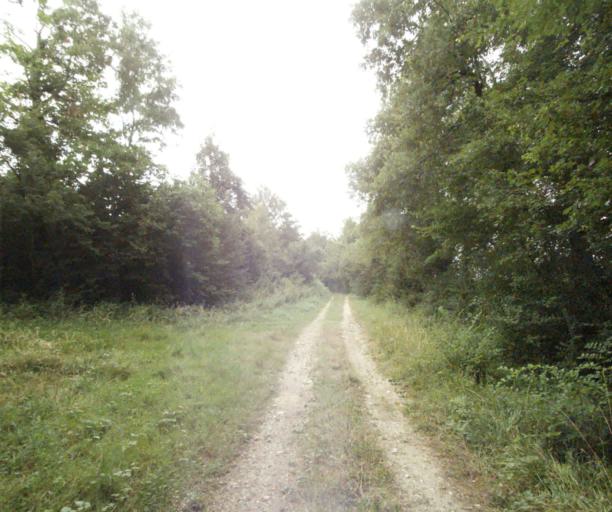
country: FR
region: Midi-Pyrenees
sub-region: Departement du Tarn
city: Soreze
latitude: 43.4572
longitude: 2.0870
